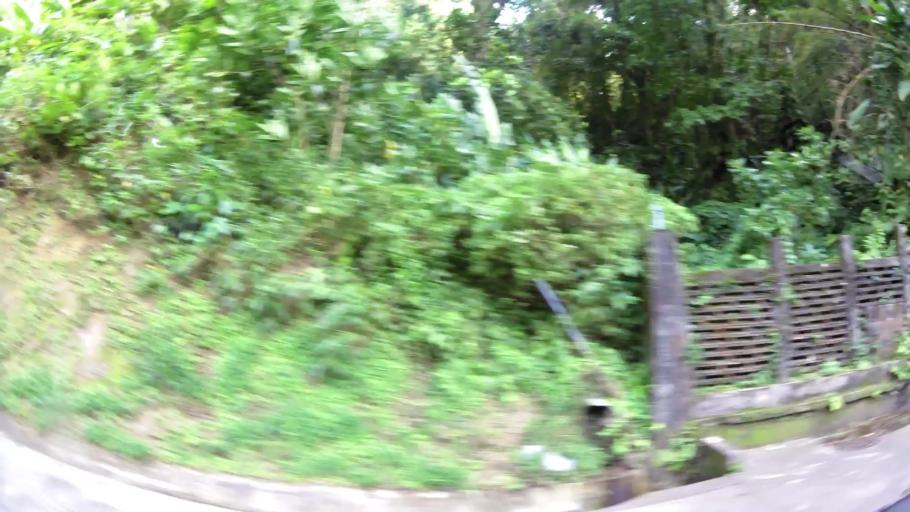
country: MQ
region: Martinique
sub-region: Martinique
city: Saint-Joseph
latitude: 14.6762
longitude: -61.0879
